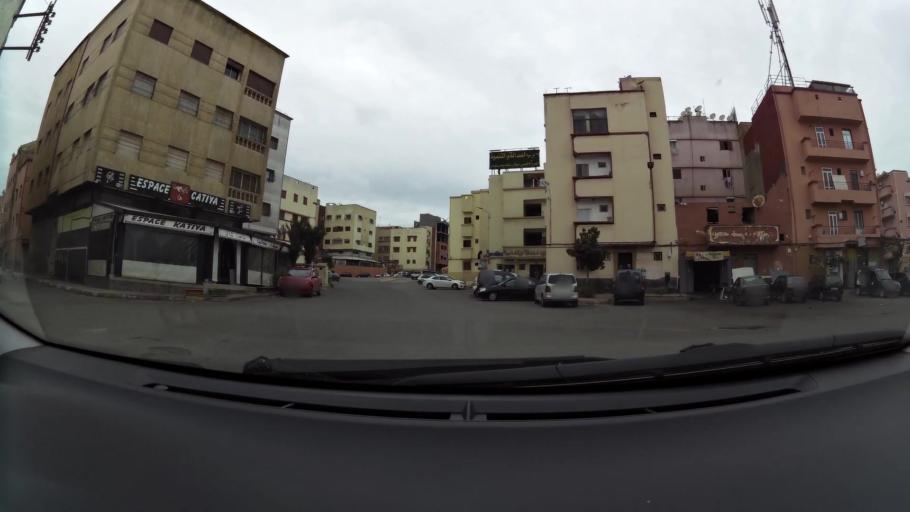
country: MA
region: Grand Casablanca
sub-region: Mediouna
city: Tit Mellil
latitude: 33.5695
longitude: -7.5495
